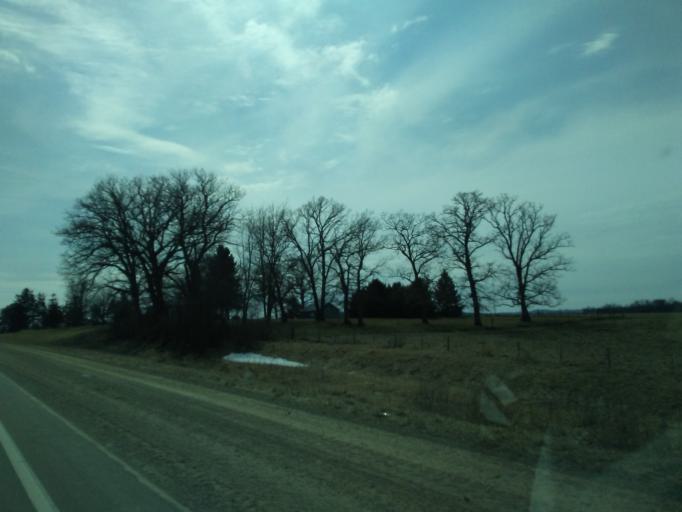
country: US
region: Iowa
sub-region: Winneshiek County
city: Decorah
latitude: 43.4234
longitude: -91.8592
